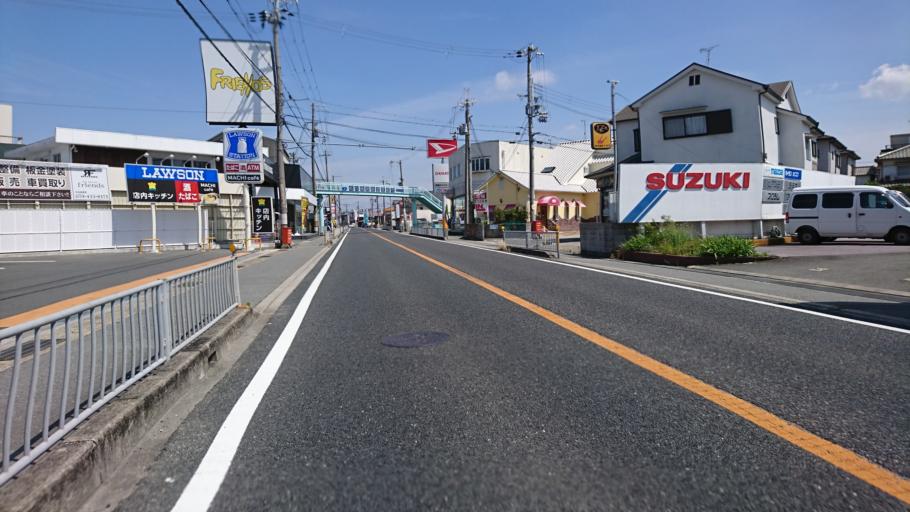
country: JP
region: Hyogo
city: Kakogawacho-honmachi
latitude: 34.7787
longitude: 134.8200
